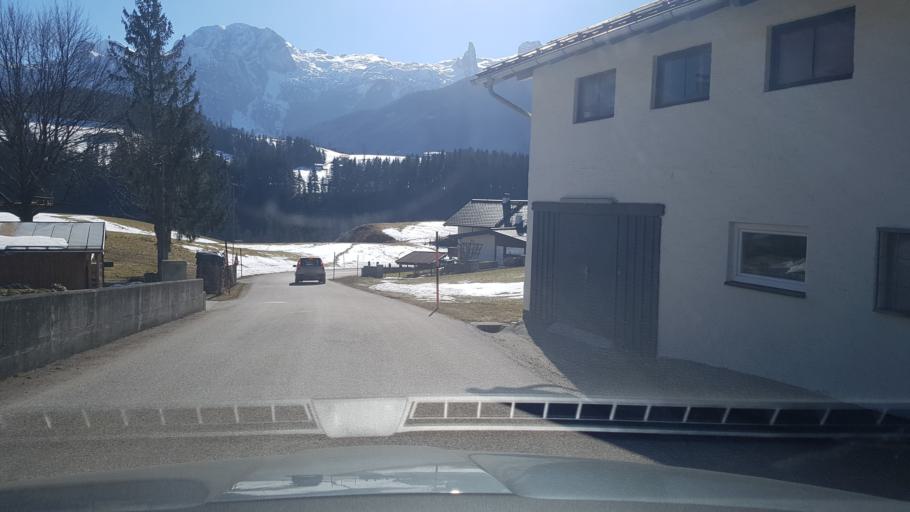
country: AT
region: Salzburg
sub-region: Politischer Bezirk Hallein
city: Abtenau
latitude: 47.5956
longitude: 13.3326
